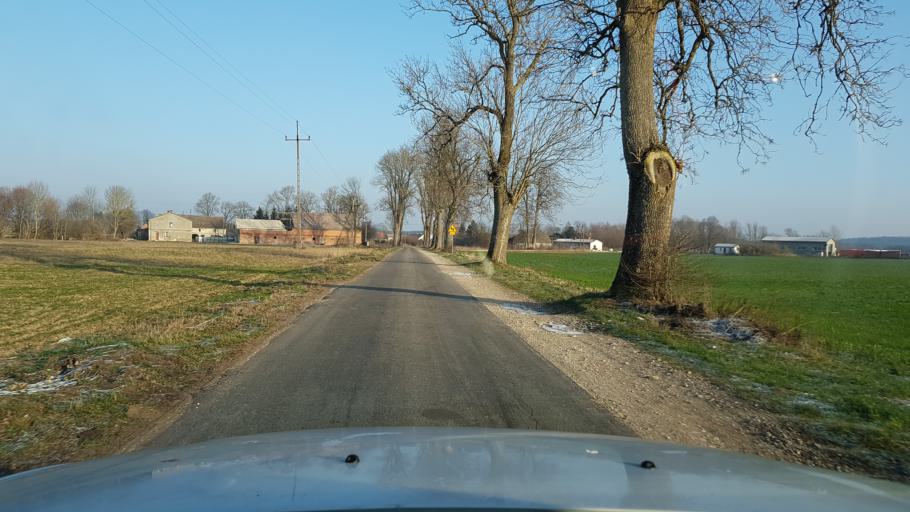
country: PL
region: West Pomeranian Voivodeship
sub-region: Powiat bialogardzki
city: Bialogard
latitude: 54.0673
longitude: 16.0856
